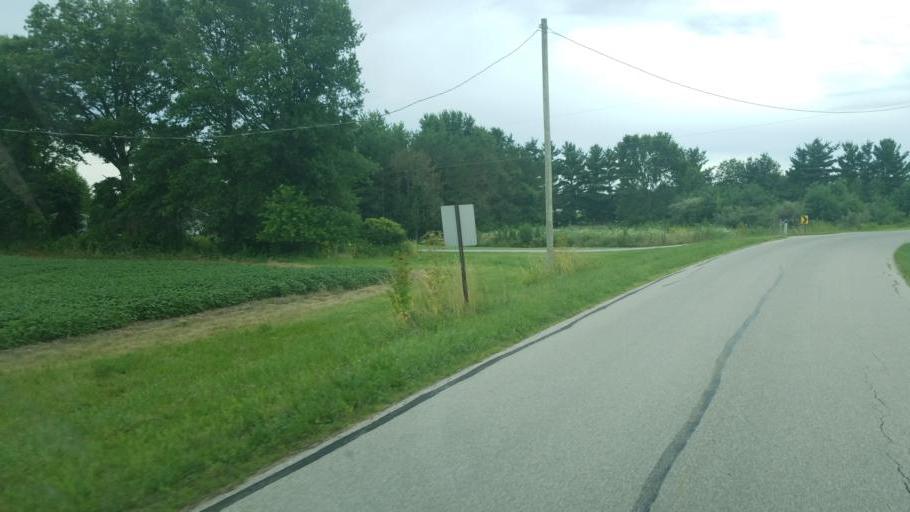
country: US
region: Ohio
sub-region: Delaware County
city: Sunbury
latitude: 40.3116
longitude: -82.9121
